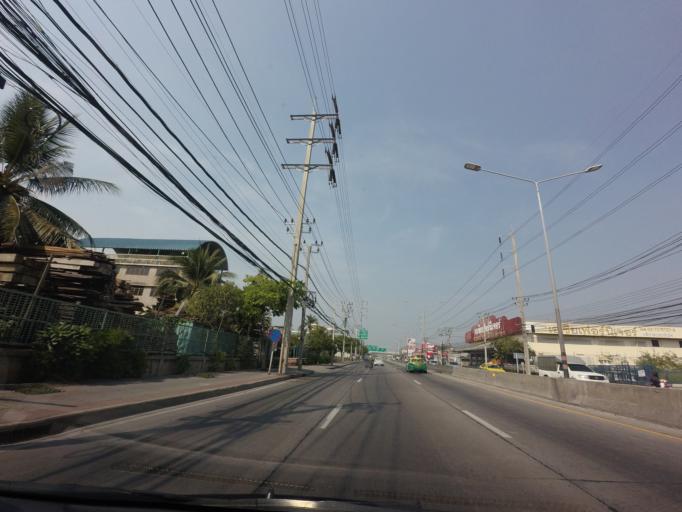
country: TH
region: Bangkok
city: Lat Krabang
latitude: 13.7518
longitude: 100.7464
